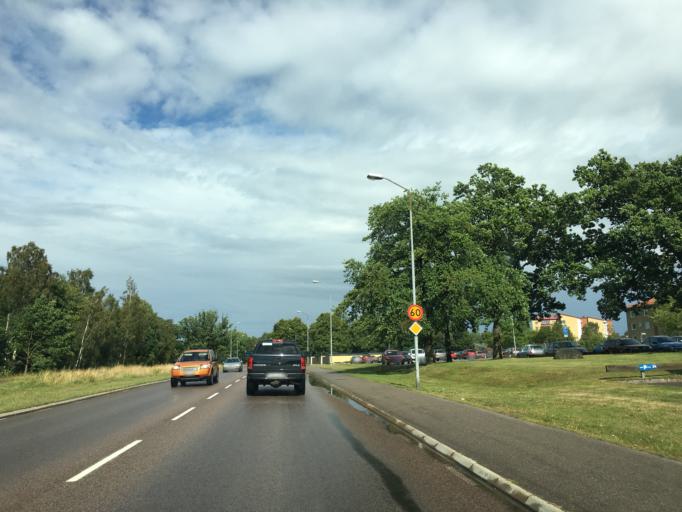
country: SE
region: Kalmar
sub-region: Kalmar Kommun
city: Kalmar
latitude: 56.6964
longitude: 16.3351
